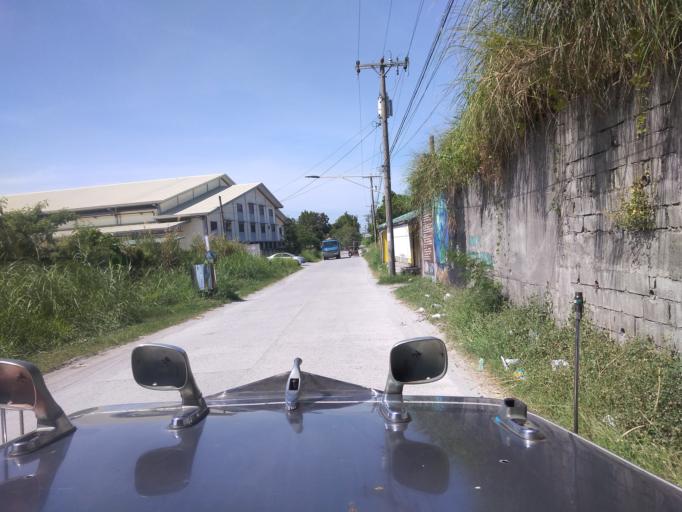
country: PH
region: Central Luzon
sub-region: Province of Pampanga
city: Bacolor
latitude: 15.0154
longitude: 120.6606
